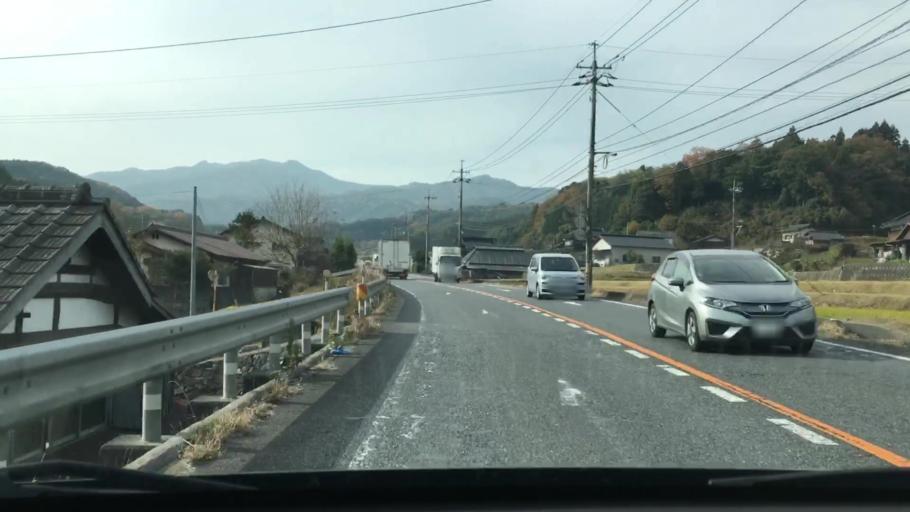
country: JP
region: Yamaguchi
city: Hikari
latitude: 34.0932
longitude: 132.0240
